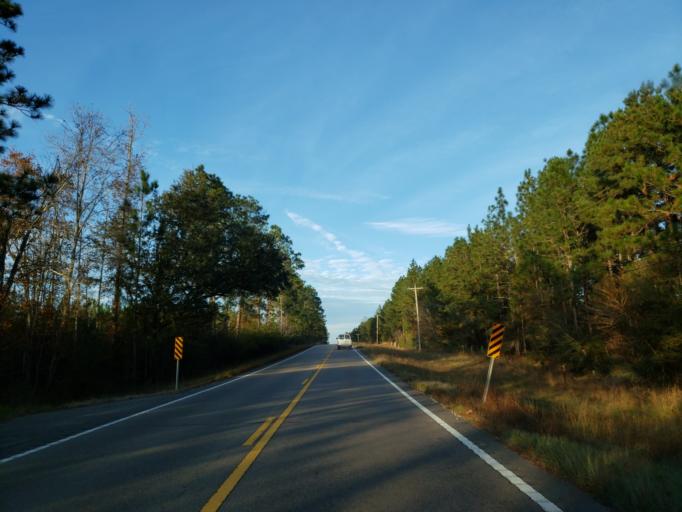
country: US
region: Mississippi
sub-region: Lamar County
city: Purvis
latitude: 31.2171
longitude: -89.3586
